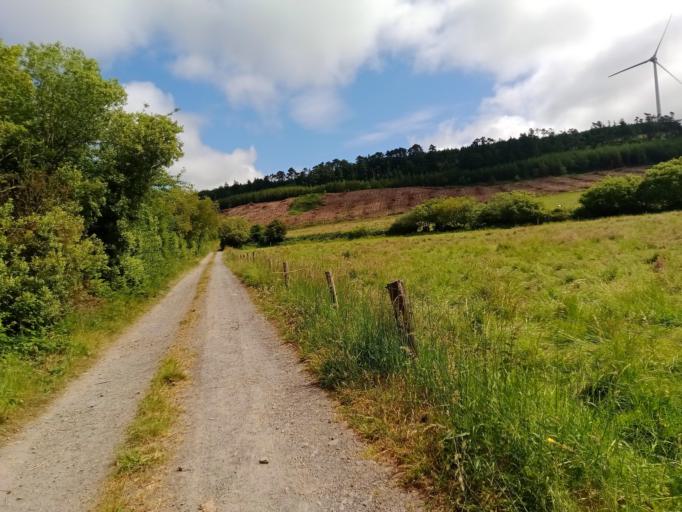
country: IE
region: Leinster
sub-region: Kilkenny
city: Ballyragget
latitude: 52.7850
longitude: -7.4480
